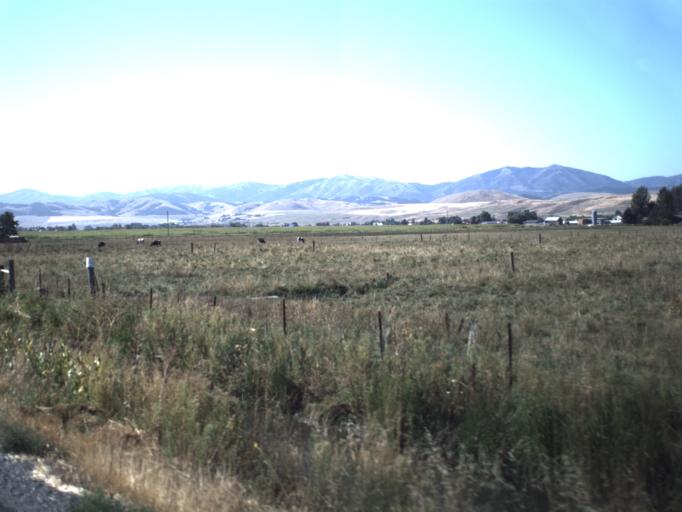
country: US
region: Utah
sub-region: Cache County
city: Hyrum
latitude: 41.6155
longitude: -111.8328
